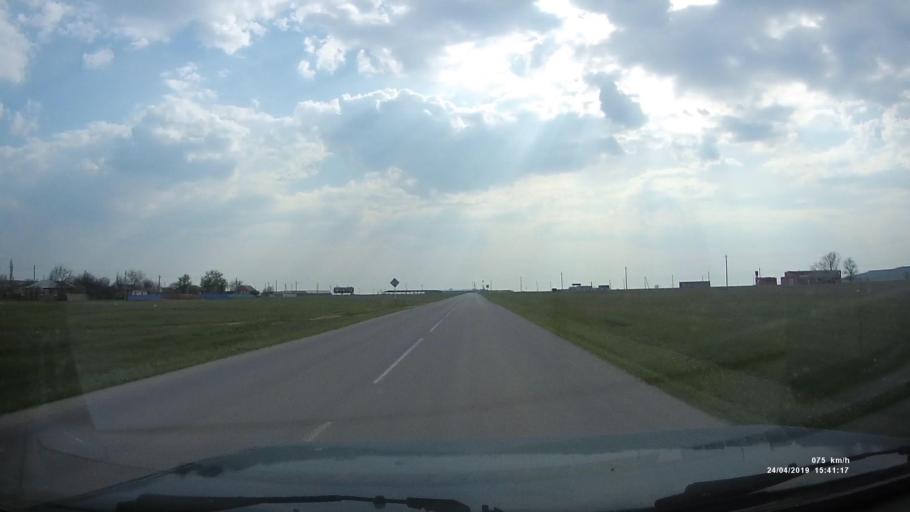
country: RU
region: Kalmykiya
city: Yashalta
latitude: 46.5728
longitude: 42.7990
